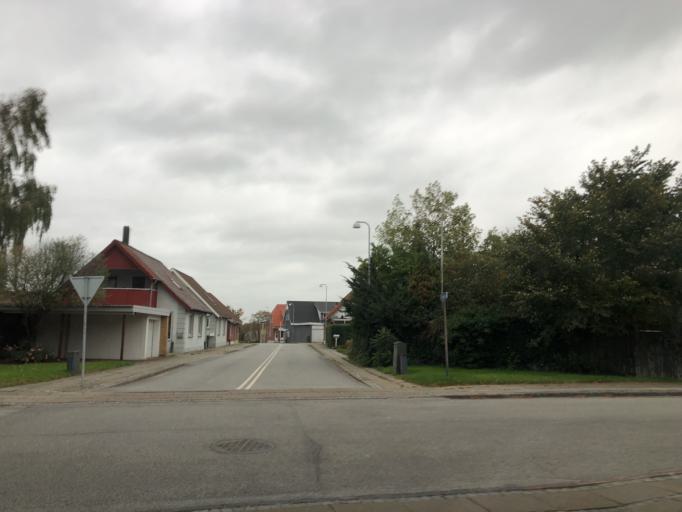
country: DK
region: Central Jutland
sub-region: Herning Kommune
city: Avlum
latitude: 56.2649
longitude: 8.7938
